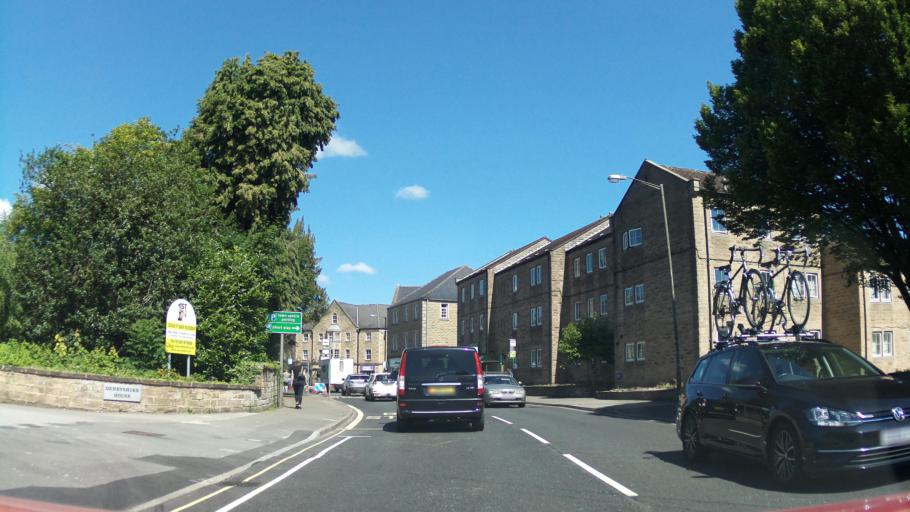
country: GB
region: England
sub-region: Derbyshire
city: Bakewell
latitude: 53.2114
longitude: -1.6742
